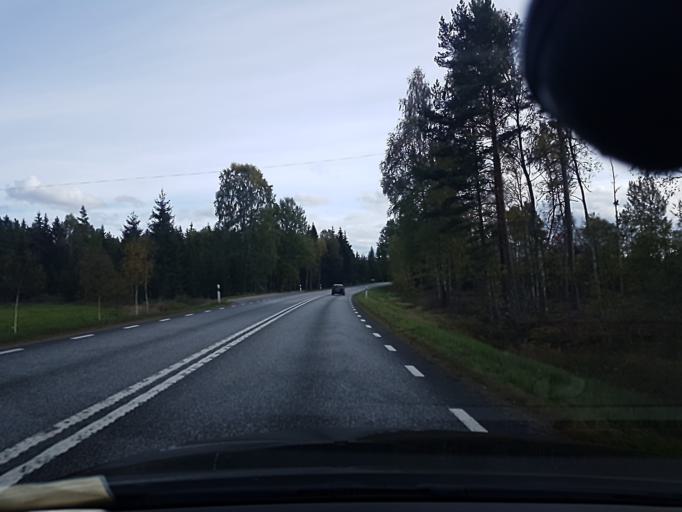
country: SE
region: Joenkoeping
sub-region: Varnamo Kommun
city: Bredaryd
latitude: 57.1765
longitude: 13.7606
